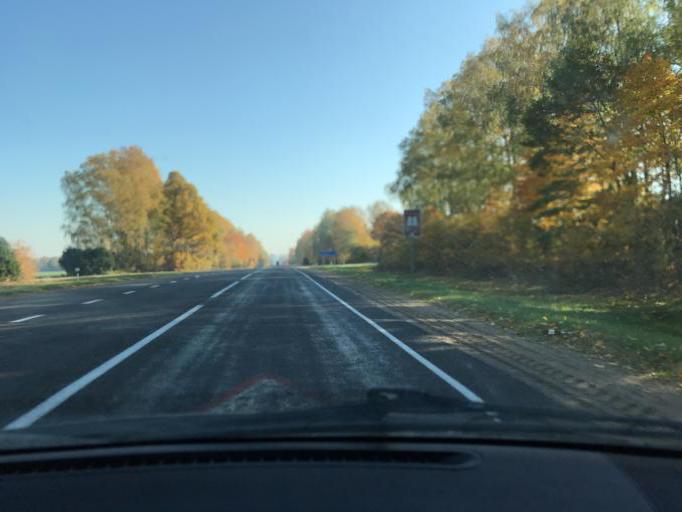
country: BY
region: Brest
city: Lyakhavichy
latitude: 52.9566
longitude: 26.3119
